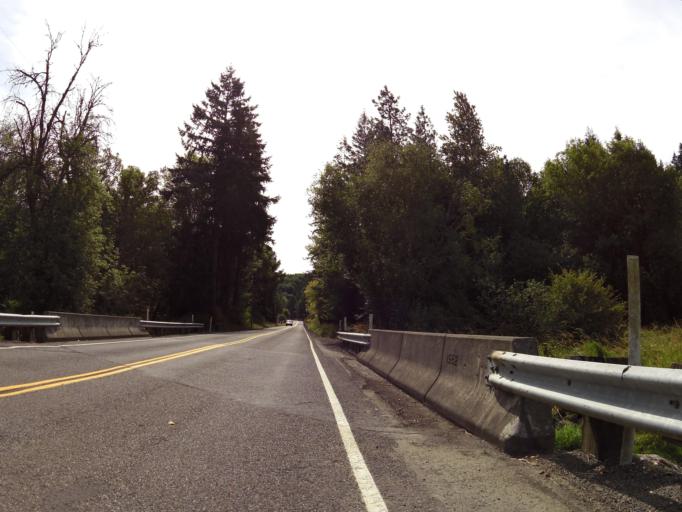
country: US
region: Washington
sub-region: Lewis County
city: Napavine
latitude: 46.5659
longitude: -122.9660
